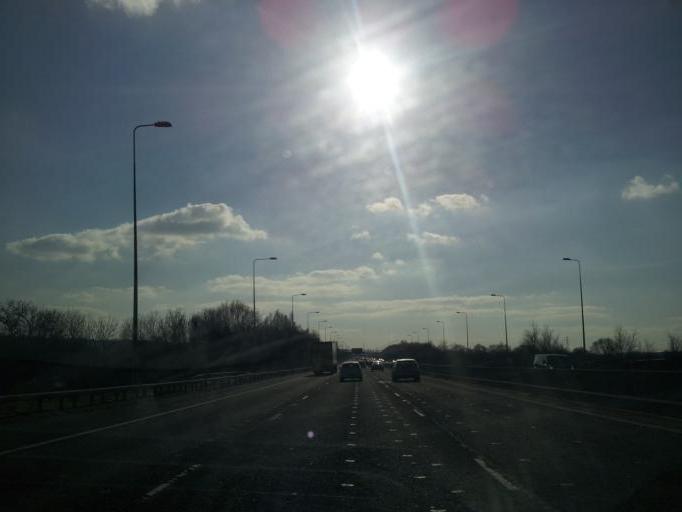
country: GB
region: England
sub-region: South Gloucestershire
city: Severn Beach
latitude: 51.5127
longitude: -2.6523
